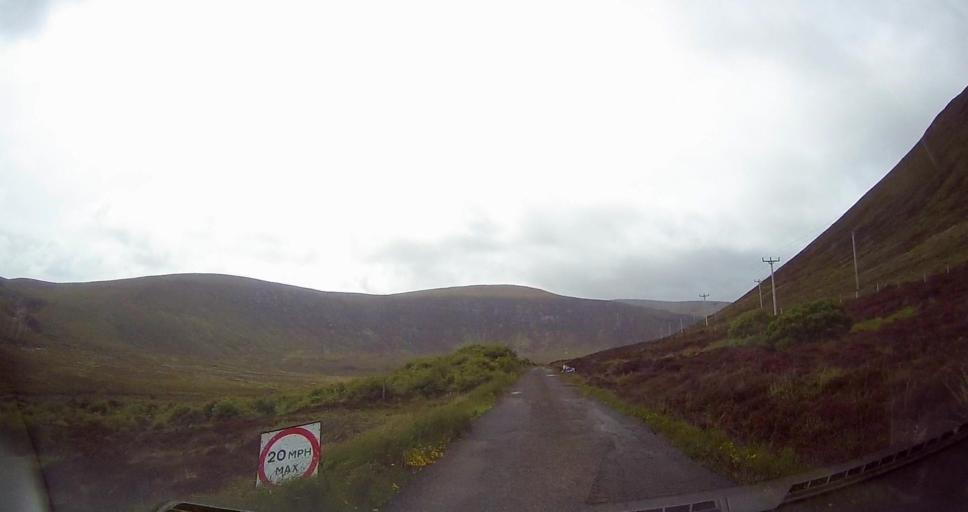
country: GB
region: Scotland
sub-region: Orkney Islands
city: Stromness
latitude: 58.8970
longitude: -3.3143
